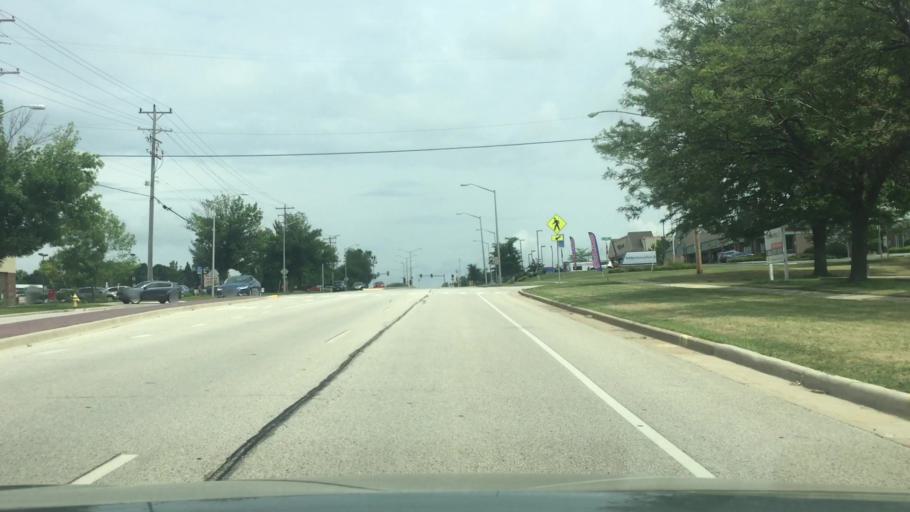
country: US
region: Wisconsin
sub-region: Waukesha County
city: Waukesha
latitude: 42.9883
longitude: -88.2248
